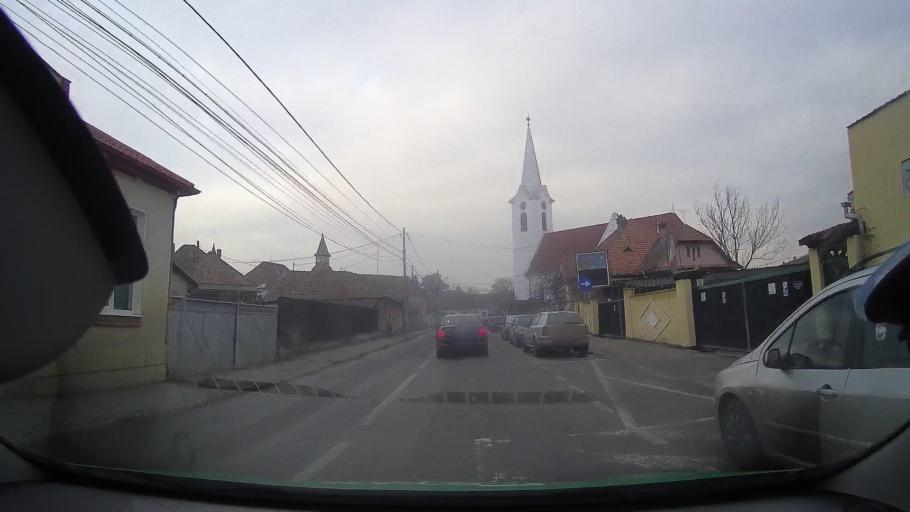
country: RO
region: Mures
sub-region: Comuna Ludus
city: Ludus
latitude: 46.4842
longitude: 24.0955
